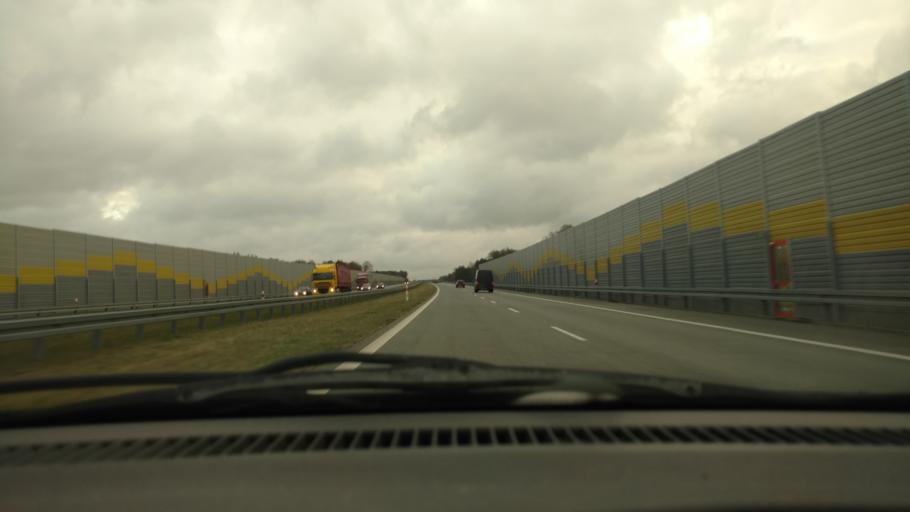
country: PL
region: Lodz Voivodeship
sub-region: Powiat lodzki wschodni
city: Rzgow
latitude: 51.6333
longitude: 19.4654
